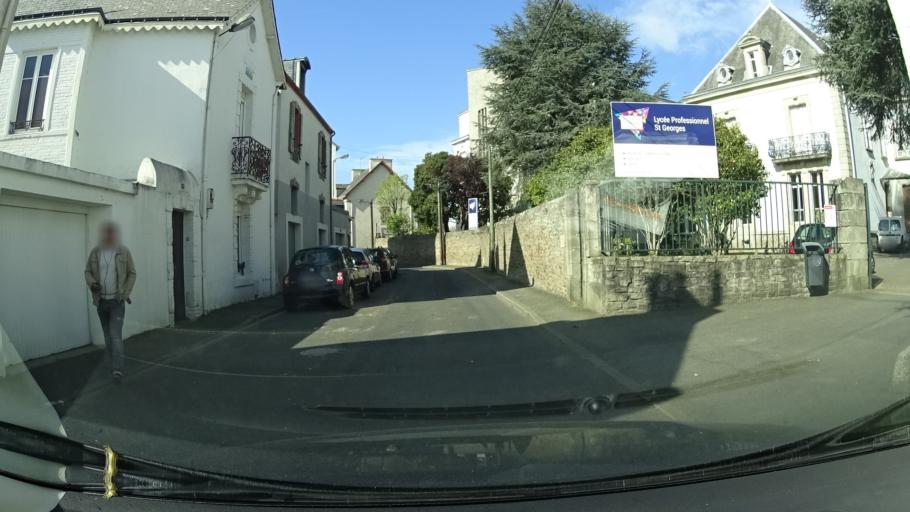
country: FR
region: Brittany
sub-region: Departement du Morbihan
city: Vannes
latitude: 47.6528
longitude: -2.7663
